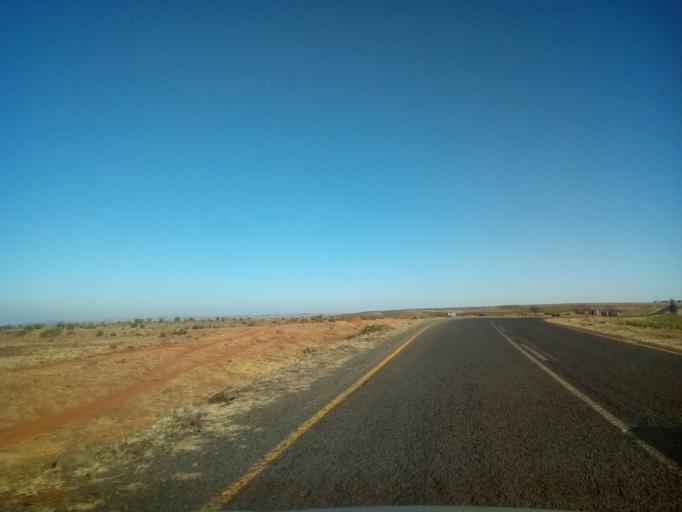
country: LS
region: Berea
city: Teyateyaneng
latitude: -29.2572
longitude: 27.7517
